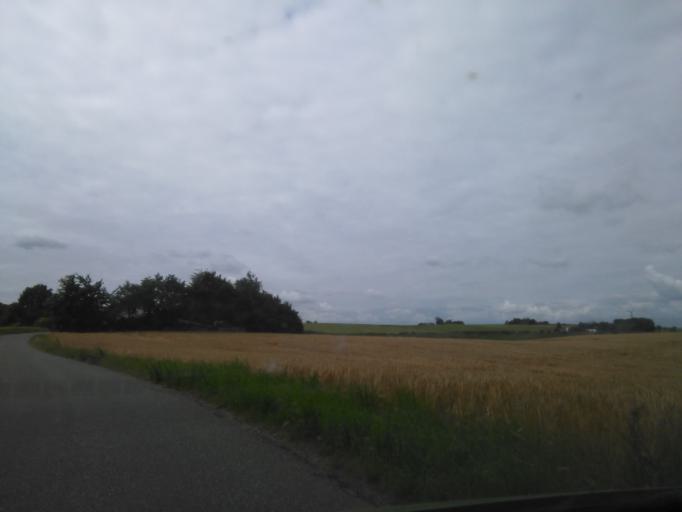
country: DK
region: Central Jutland
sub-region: Arhus Kommune
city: Solbjerg
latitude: 56.0173
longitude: 10.0716
